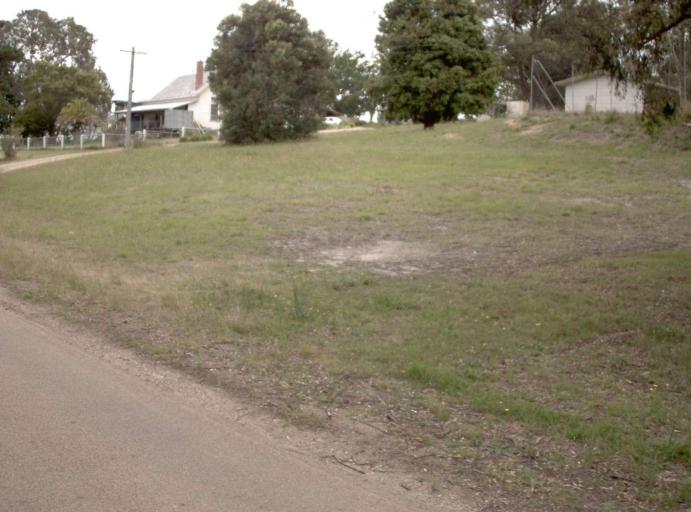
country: AU
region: Victoria
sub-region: East Gippsland
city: Bairnsdale
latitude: -37.7444
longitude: 147.5982
